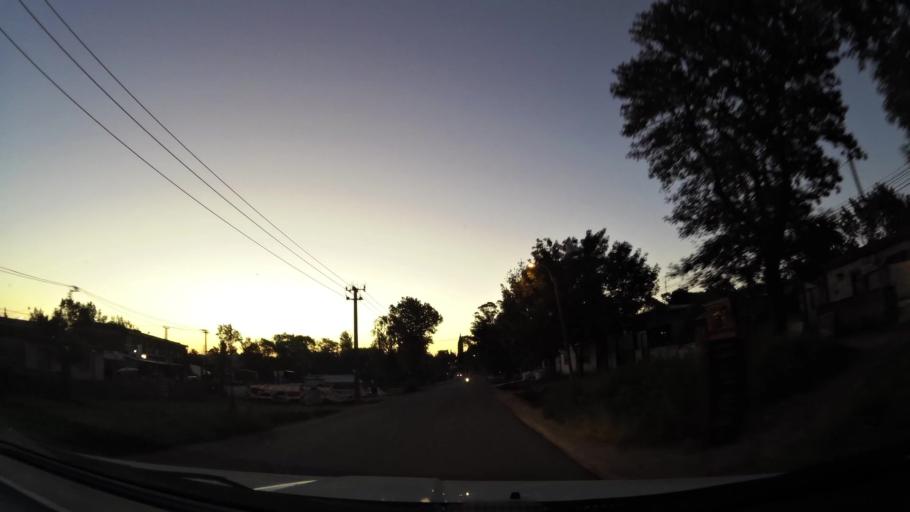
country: UY
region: Canelones
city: La Paz
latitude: -34.8253
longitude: -56.1788
